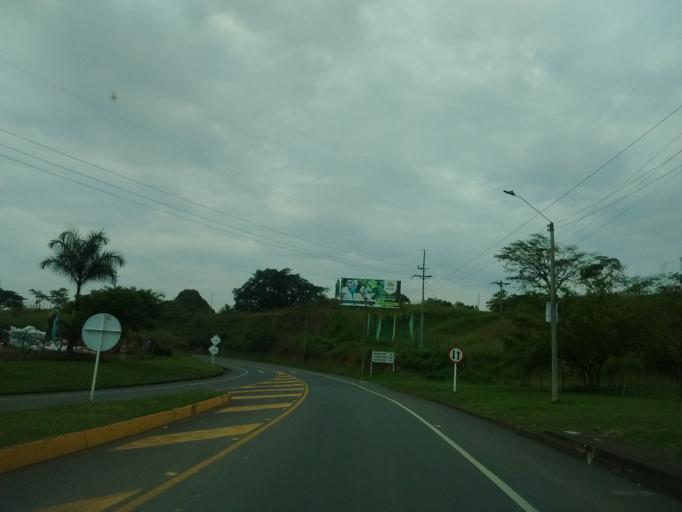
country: CO
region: Cauca
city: Santander de Quilichao
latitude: 3.0270
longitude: -76.4997
